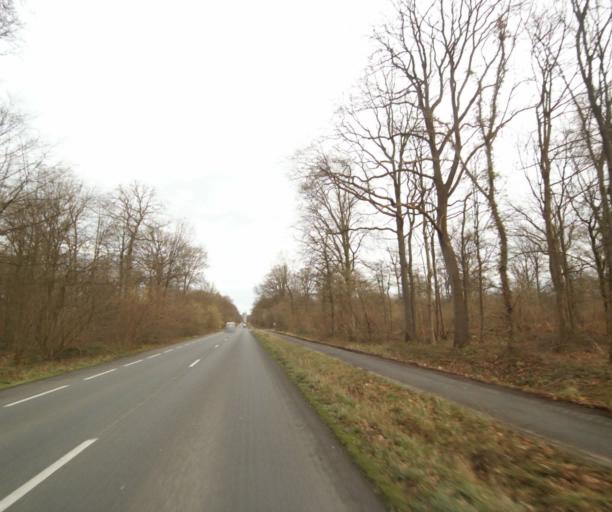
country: FR
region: Nord-Pas-de-Calais
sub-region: Departement du Nord
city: Conde-sur-l'Escaut
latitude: 50.4772
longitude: 3.5996
